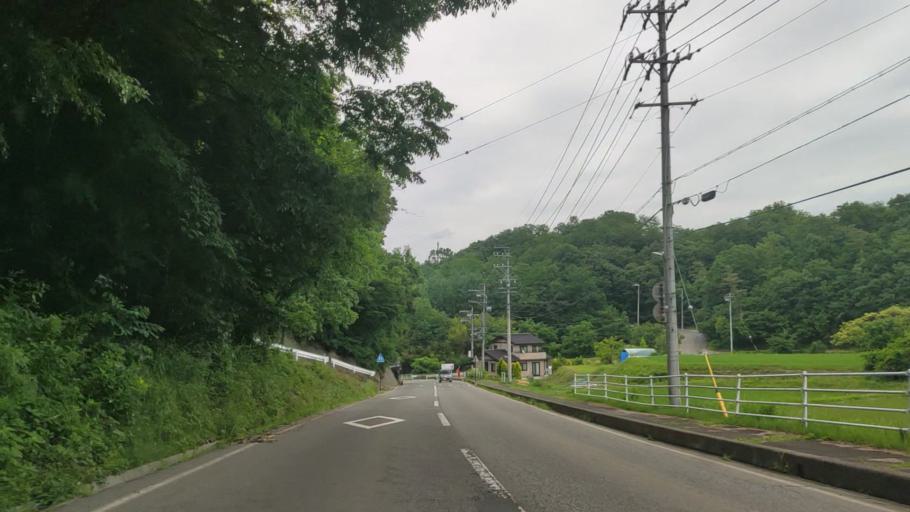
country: JP
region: Nagano
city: Kamimaruko
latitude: 36.3002
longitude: 138.3225
